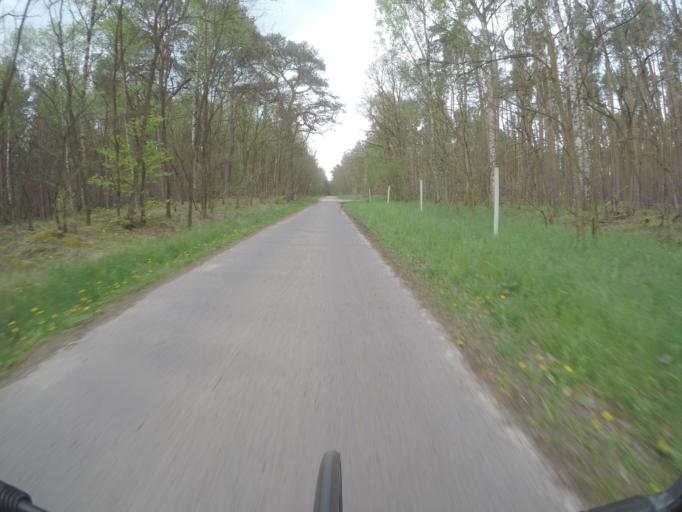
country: DE
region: Brandenburg
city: Biesenthal
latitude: 52.7849
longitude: 13.6378
